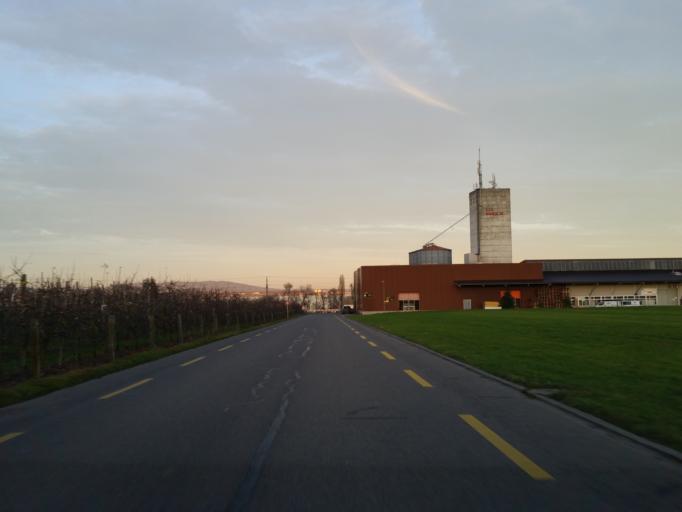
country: CH
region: Thurgau
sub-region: Kreuzlingen District
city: Guttingen
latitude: 47.6092
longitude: 9.2874
